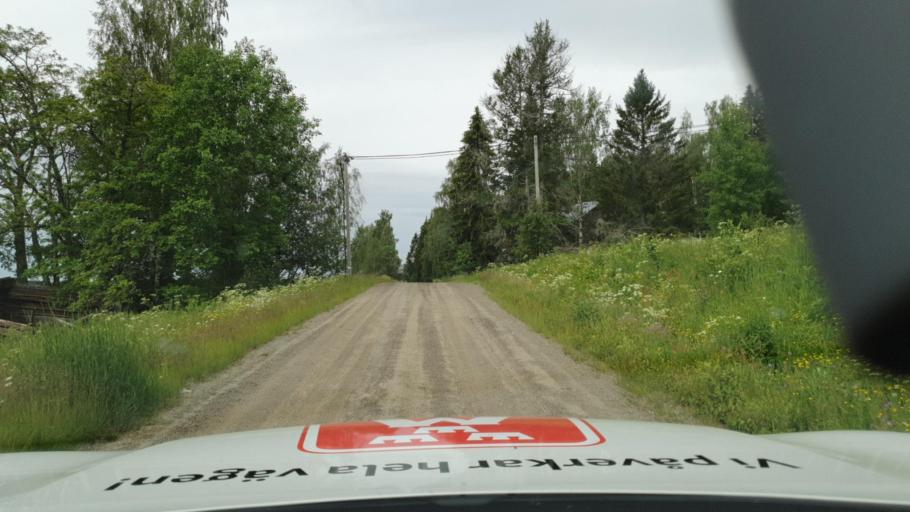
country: SE
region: Vaesterbotten
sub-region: Robertsfors Kommun
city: Robertsfors
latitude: 64.2842
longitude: 20.6705
